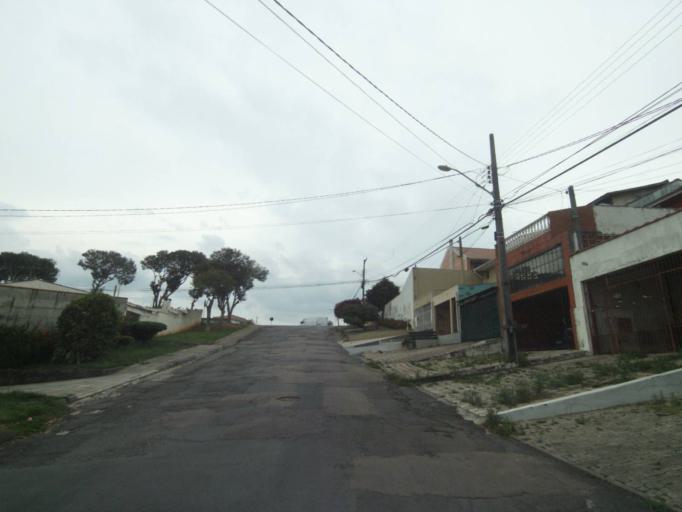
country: BR
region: Parana
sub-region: Pinhais
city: Pinhais
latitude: -25.4007
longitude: -49.2054
